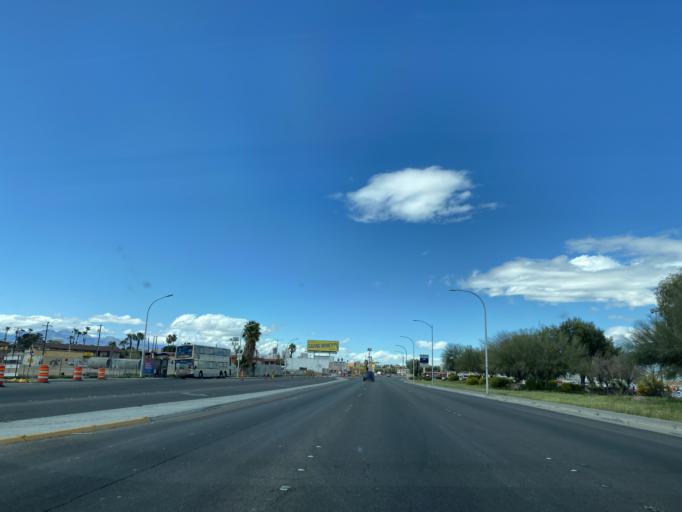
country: US
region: Nevada
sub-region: Clark County
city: Winchester
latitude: 36.1556
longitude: -115.1125
